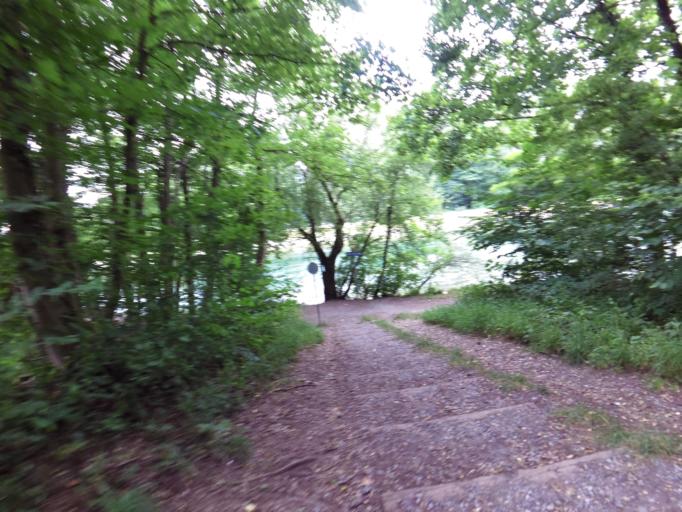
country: CH
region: Zurich
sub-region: Bezirk Zuerich
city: Zuerich (Kreis 10) / Ruetihof
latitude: 47.4034
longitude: 8.4822
